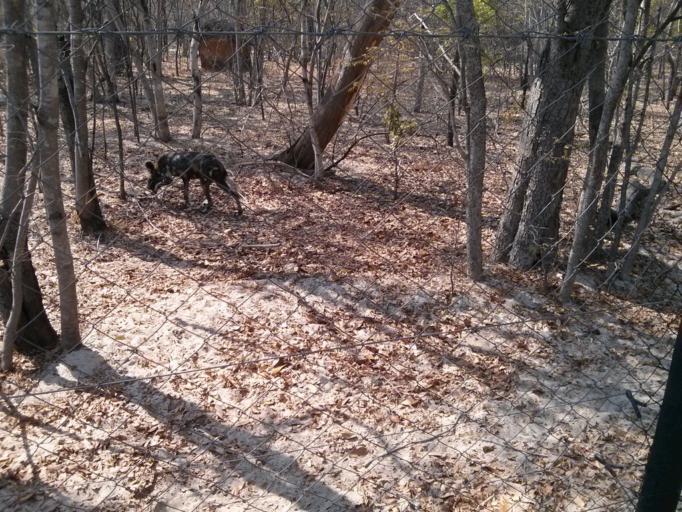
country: ZW
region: Matabeleland North
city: Dete
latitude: -18.6171
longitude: 27.0583
